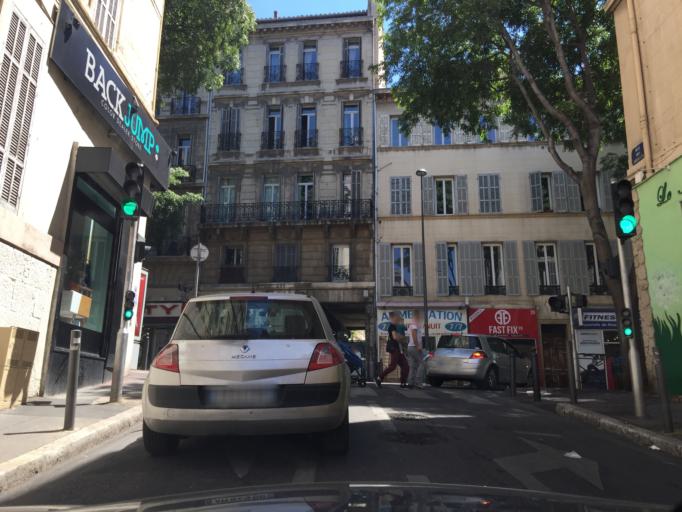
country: FR
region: Provence-Alpes-Cote d'Azur
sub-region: Departement des Bouches-du-Rhone
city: Marseille 01
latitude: 43.2999
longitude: 5.3872
